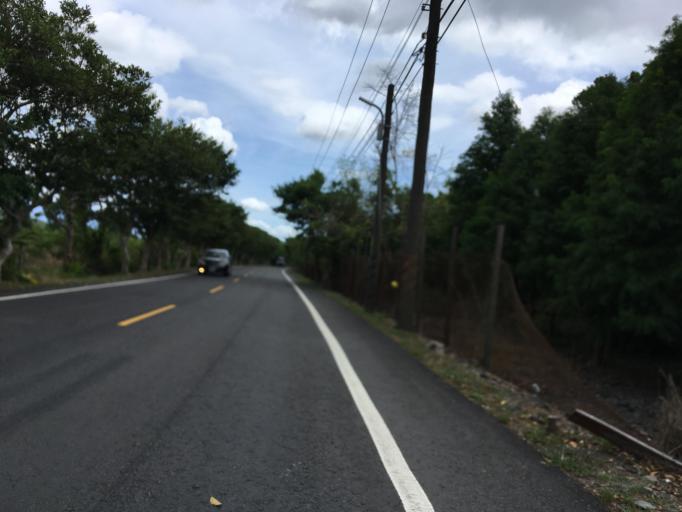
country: TW
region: Taiwan
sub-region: Yilan
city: Yilan
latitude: 24.6259
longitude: 121.7096
